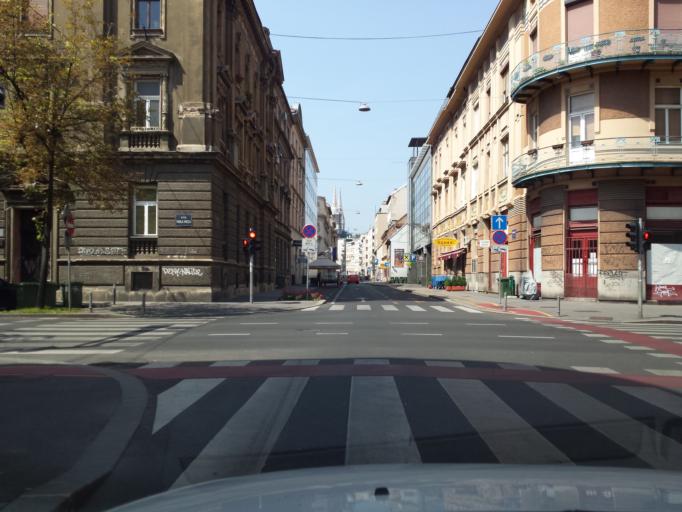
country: HR
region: Grad Zagreb
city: Zagreb - Centar
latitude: 45.8075
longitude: 15.9802
